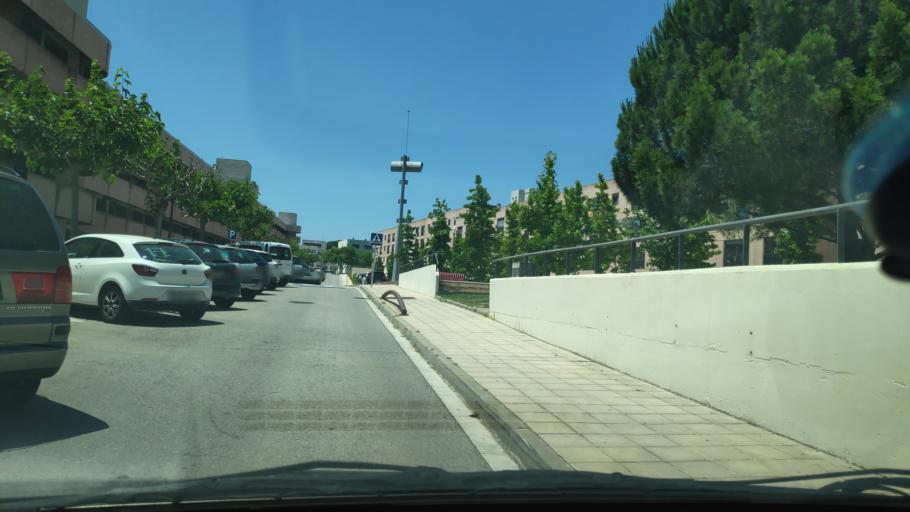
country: ES
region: Catalonia
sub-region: Provincia de Barcelona
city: Barbera del Valles
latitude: 41.4993
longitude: 2.0993
